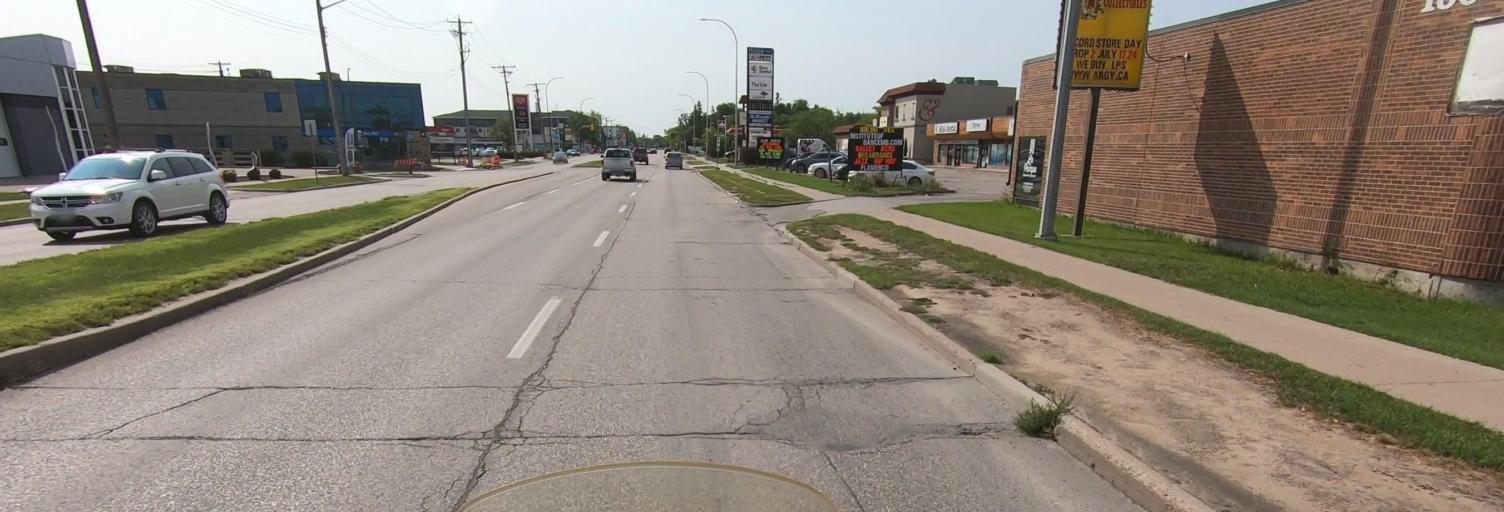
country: CA
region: Manitoba
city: Winnipeg
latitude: 49.8221
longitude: -97.1138
